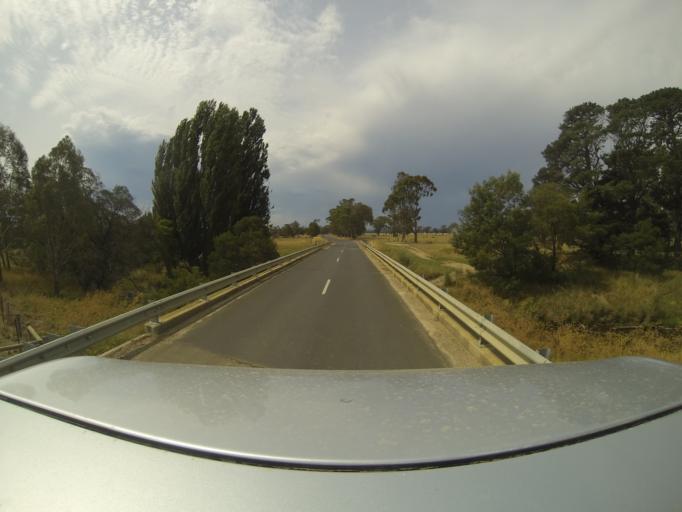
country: AU
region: Victoria
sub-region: Wellington
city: Heyfield
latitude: -37.9858
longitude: 146.6936
